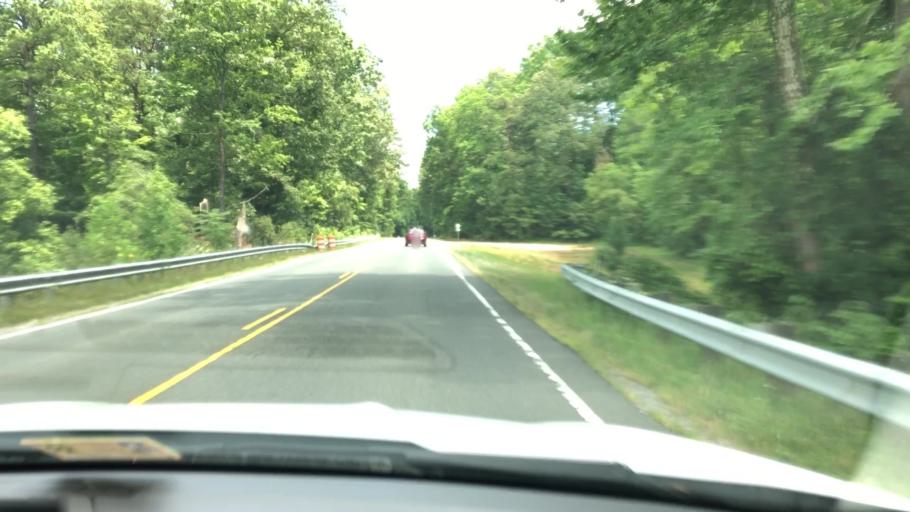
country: US
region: Virginia
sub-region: Lancaster County
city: Lancaster
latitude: 37.7696
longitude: -76.4770
